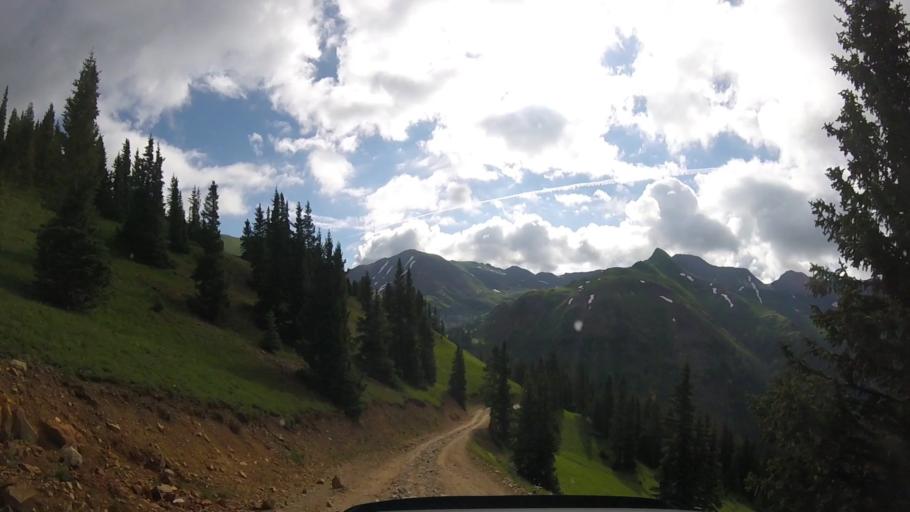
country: US
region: Colorado
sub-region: San Juan County
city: Silverton
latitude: 37.9068
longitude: -107.6538
